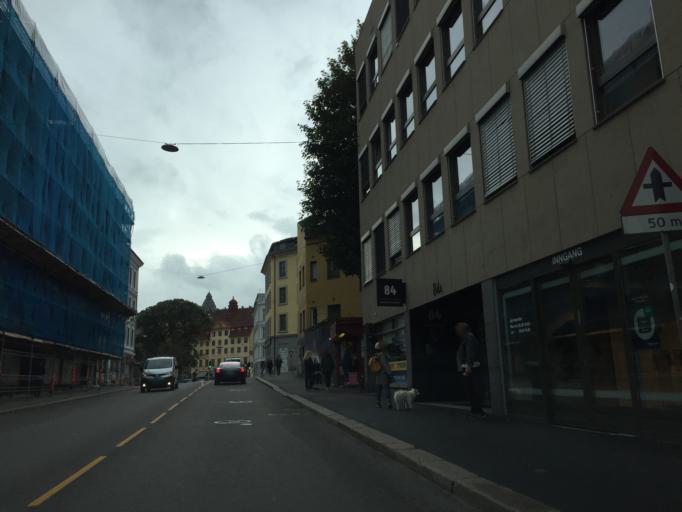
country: NO
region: Oslo
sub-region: Oslo
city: Oslo
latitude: 59.9283
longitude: 10.7530
